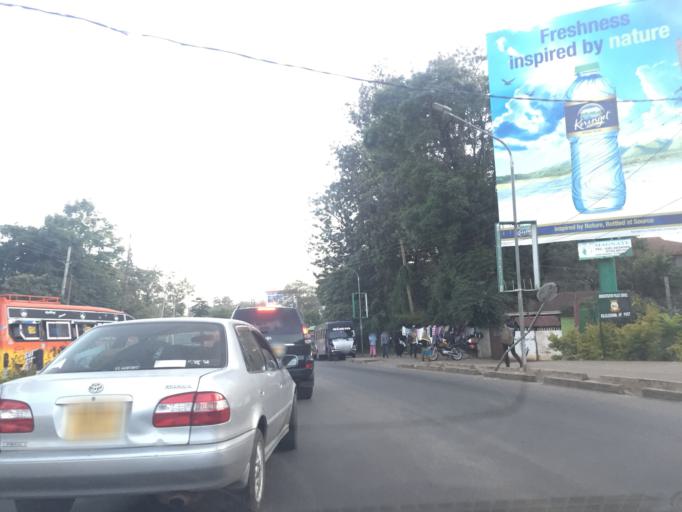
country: KE
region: Nairobi Area
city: Nairobi
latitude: -1.2665
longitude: 36.8010
